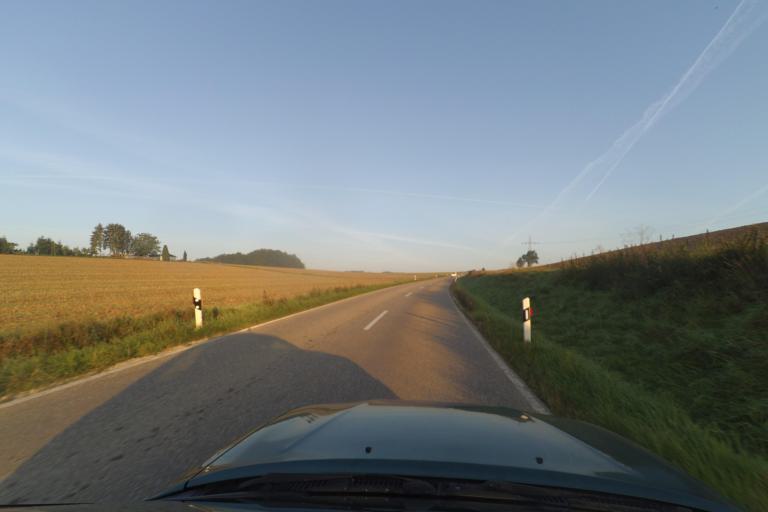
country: DE
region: Bavaria
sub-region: Lower Bavaria
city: Mainburg
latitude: 48.6509
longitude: 11.7648
